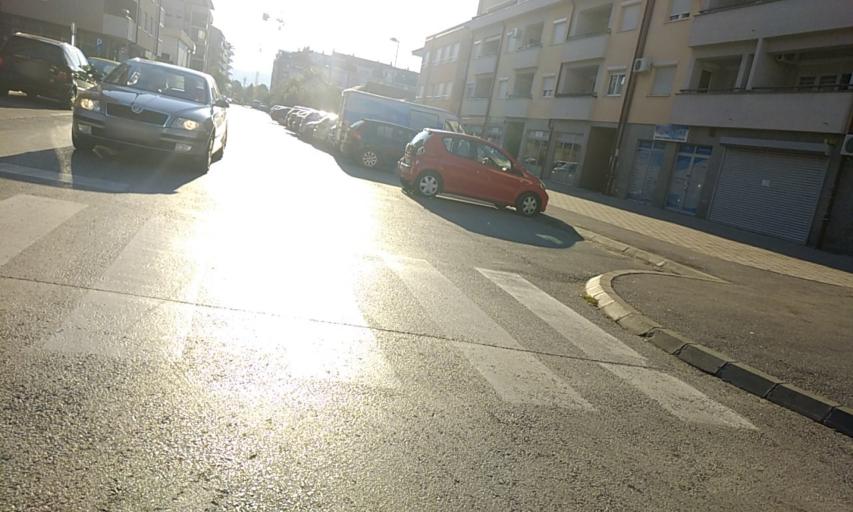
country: BA
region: Republika Srpska
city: Starcevica
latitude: 44.7636
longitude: 17.2029
